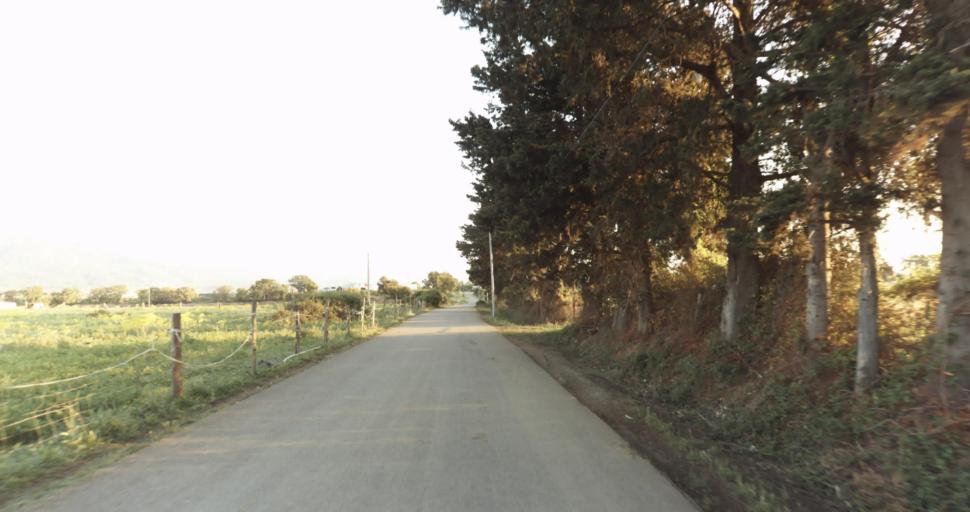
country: FR
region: Corsica
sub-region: Departement de la Haute-Corse
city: Biguglia
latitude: 42.6017
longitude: 9.4538
